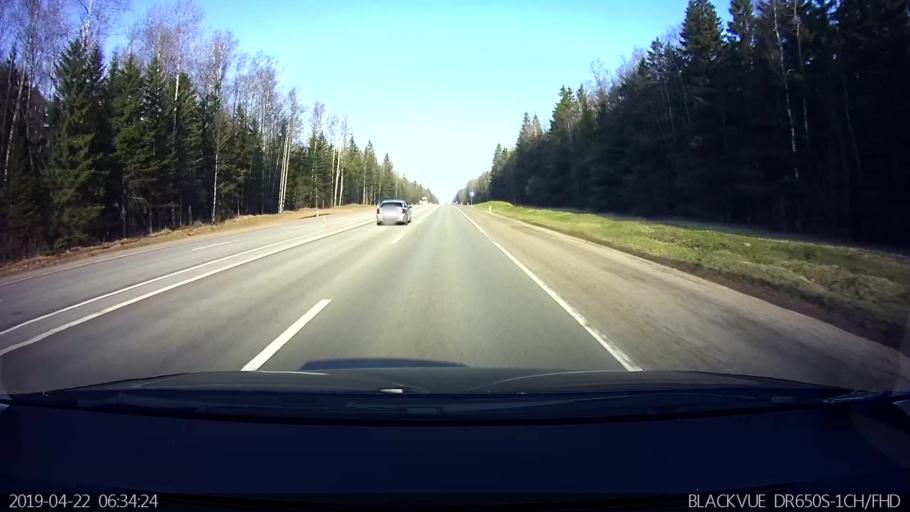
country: RU
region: Moskovskaya
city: Uvarovka
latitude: 55.4732
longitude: 35.5002
